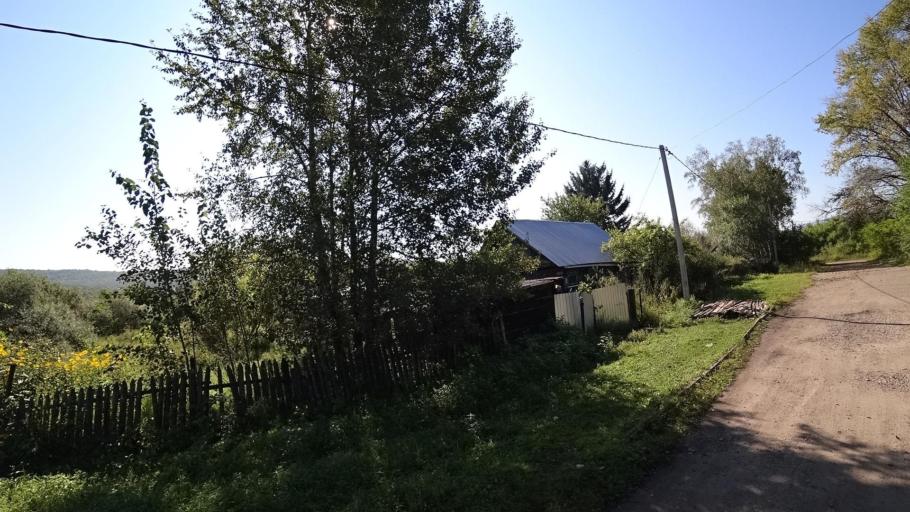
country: RU
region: Jewish Autonomous Oblast
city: Bira
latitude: 49.0033
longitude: 132.4726
